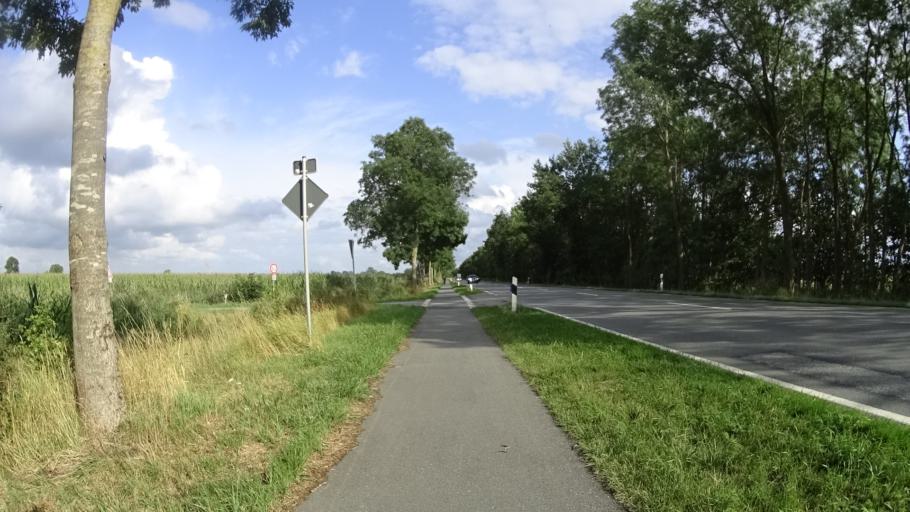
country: DE
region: Lower Saxony
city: Varel
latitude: 53.3908
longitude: 8.1896
